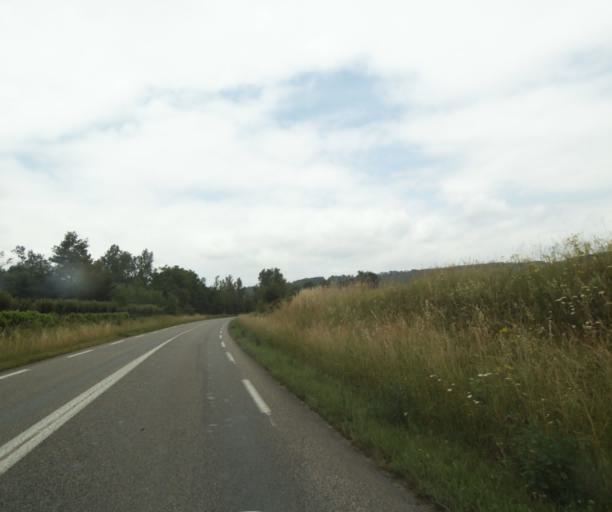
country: FR
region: Midi-Pyrenees
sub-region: Departement du Tarn-et-Garonne
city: Saint-Nauphary
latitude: 43.9822
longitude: 1.3932
